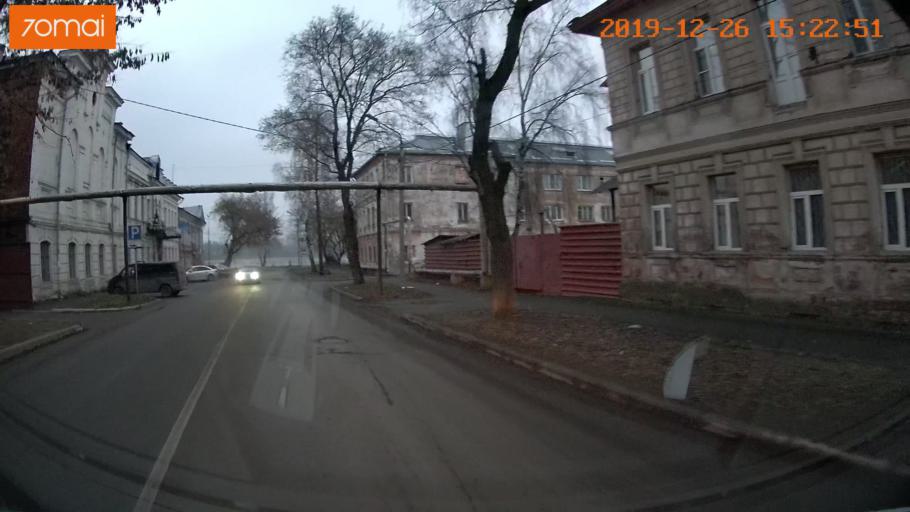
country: RU
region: Jaroslavl
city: Rybinsk
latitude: 58.0471
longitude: 38.8620
